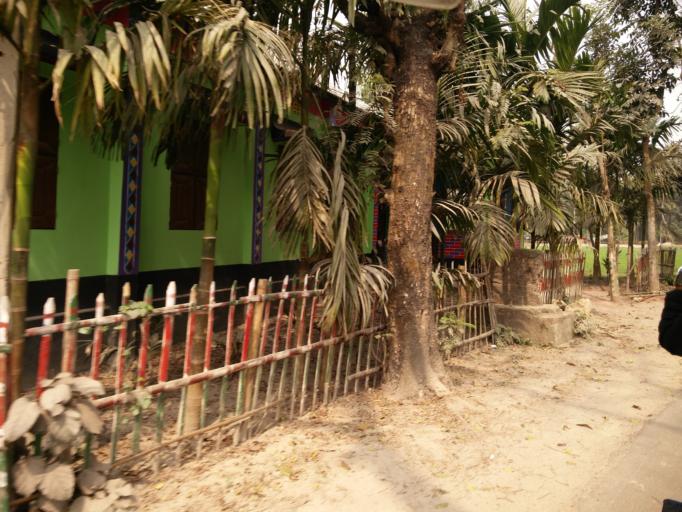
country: BD
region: Rangpur Division
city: Nageswari
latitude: 25.8839
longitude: 89.6992
